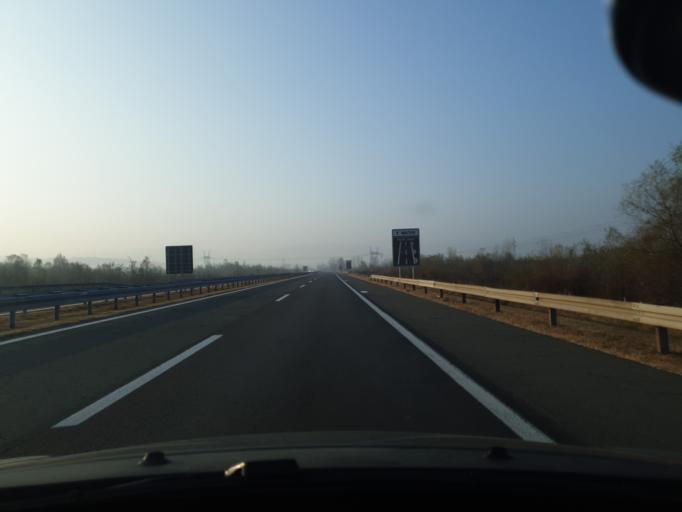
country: RS
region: Central Serbia
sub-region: Jablanicki Okrug
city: Vlasotince
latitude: 42.9615
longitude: 22.0371
